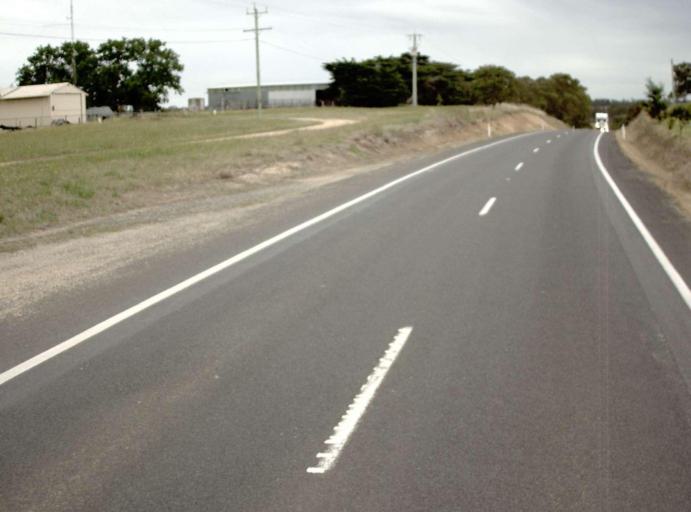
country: AU
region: Victoria
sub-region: Wellington
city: Sale
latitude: -38.2873
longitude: 147.0369
